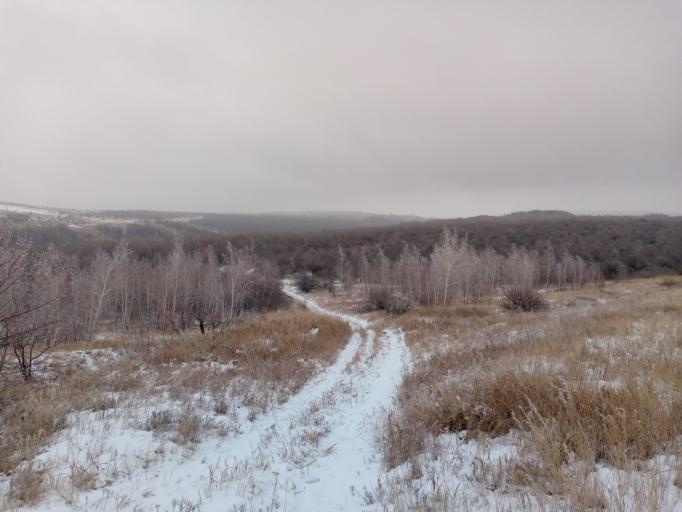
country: RU
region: Saratov
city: Krasnyy Oktyabr'
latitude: 51.3544
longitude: 45.8013
